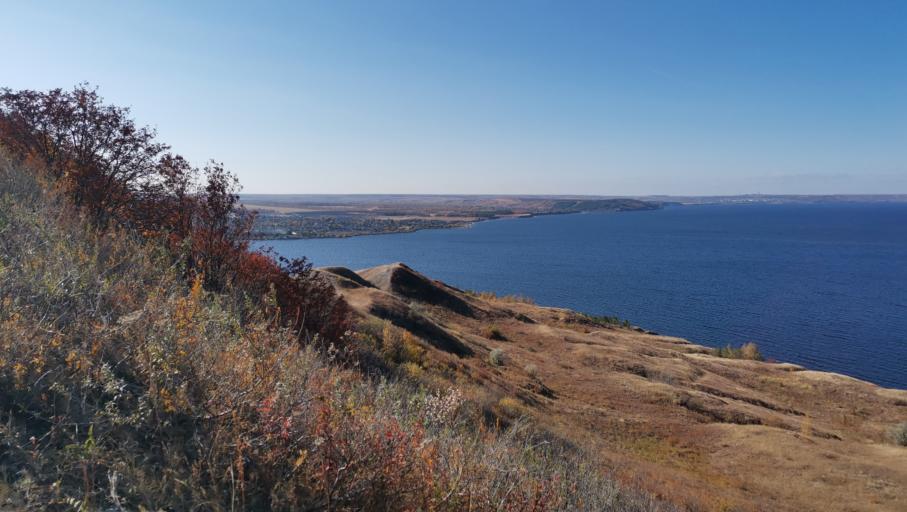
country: RU
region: Ulyanovsk
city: Novoul'yanovsk
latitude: 54.1135
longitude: 48.5695
